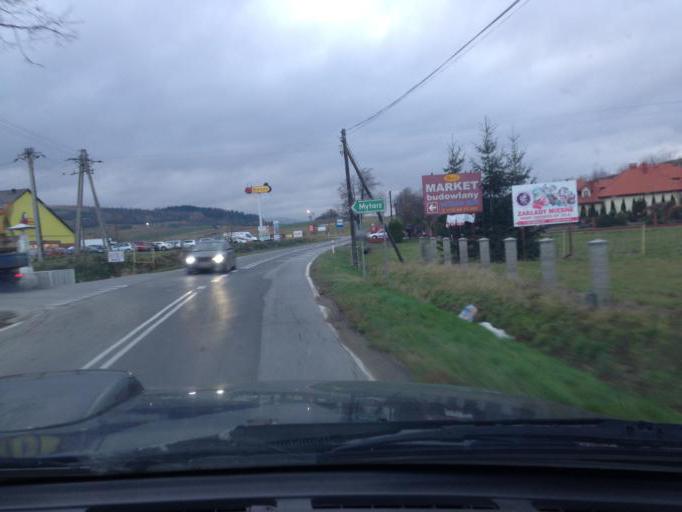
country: PL
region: Subcarpathian Voivodeship
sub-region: Powiat jasielski
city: Nowy Zmigrod
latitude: 49.6085
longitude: 21.5201
